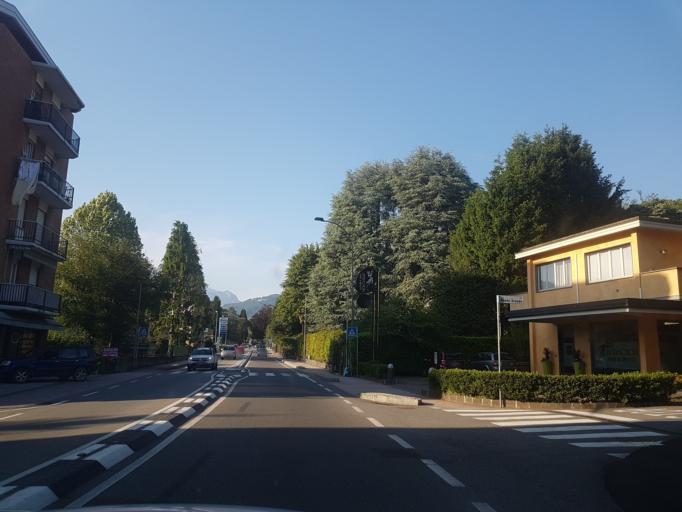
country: IT
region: Lombardy
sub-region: Provincia di Lecco
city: Oggiono
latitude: 45.7908
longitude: 9.3519
